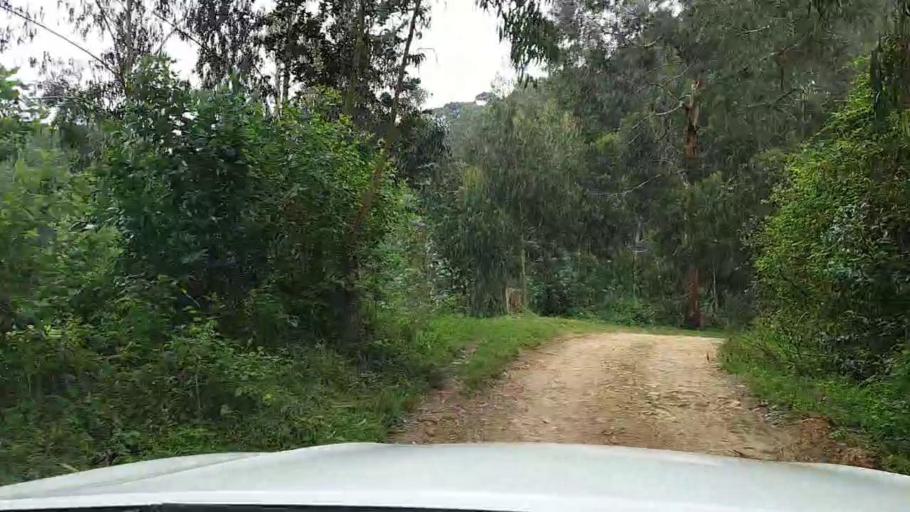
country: RW
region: Western Province
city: Kibuye
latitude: -2.2739
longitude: 29.3635
